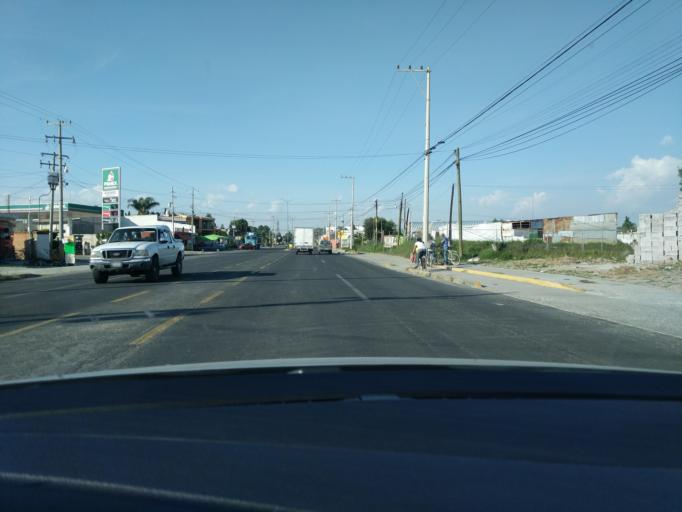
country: MX
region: Puebla
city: San Andres Cholula
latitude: 19.0383
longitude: -98.3158
